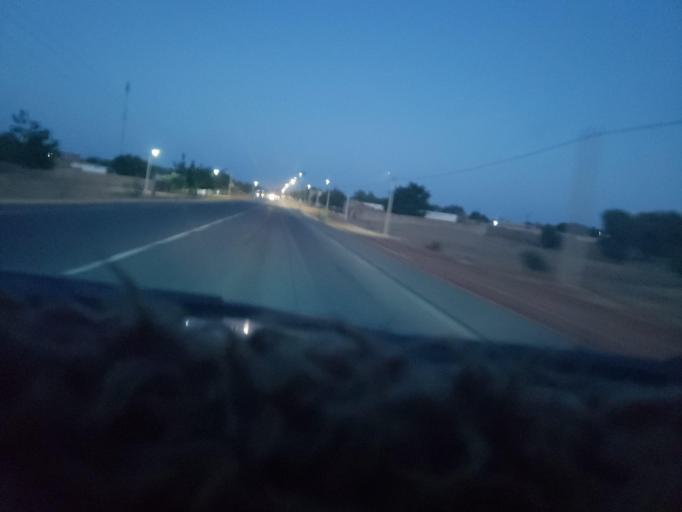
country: SN
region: Louga
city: Ndibene Dahra
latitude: 15.3824
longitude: -15.2424
